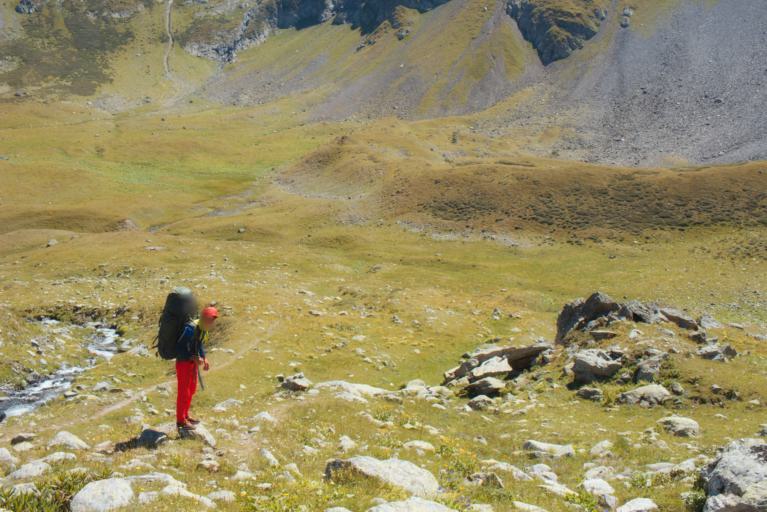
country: RU
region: Karachayevo-Cherkesiya
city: Mednogorskiy
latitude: 43.6231
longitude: 41.1152
